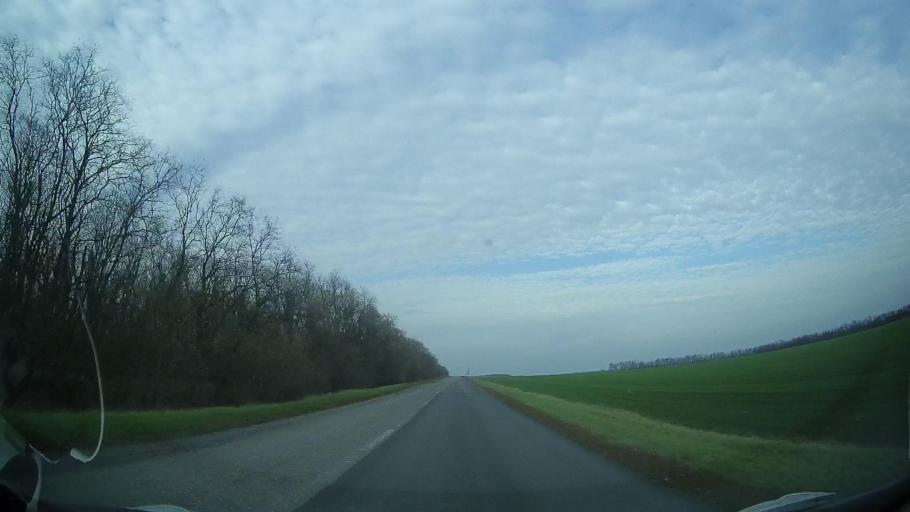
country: RU
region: Rostov
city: Zernograd
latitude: 46.9596
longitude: 40.3669
